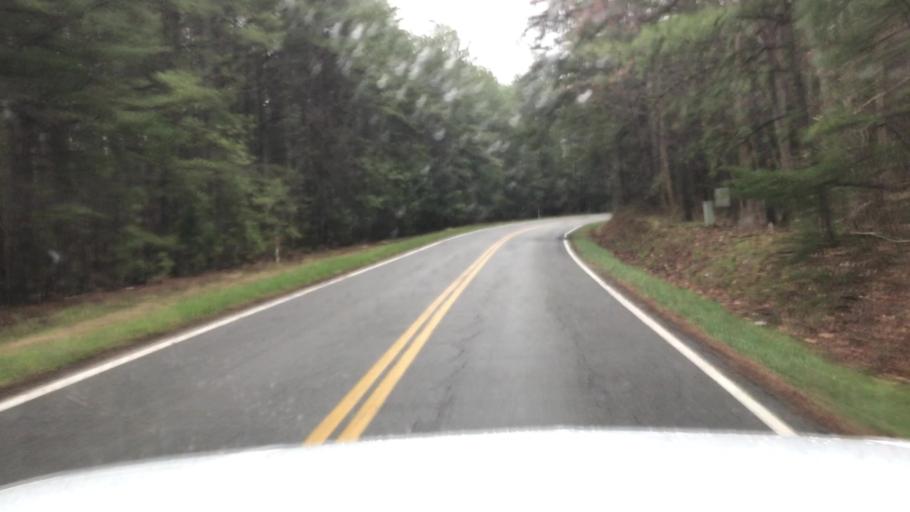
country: US
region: Virginia
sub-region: Henrico County
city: Short Pump
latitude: 37.6347
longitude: -77.6792
